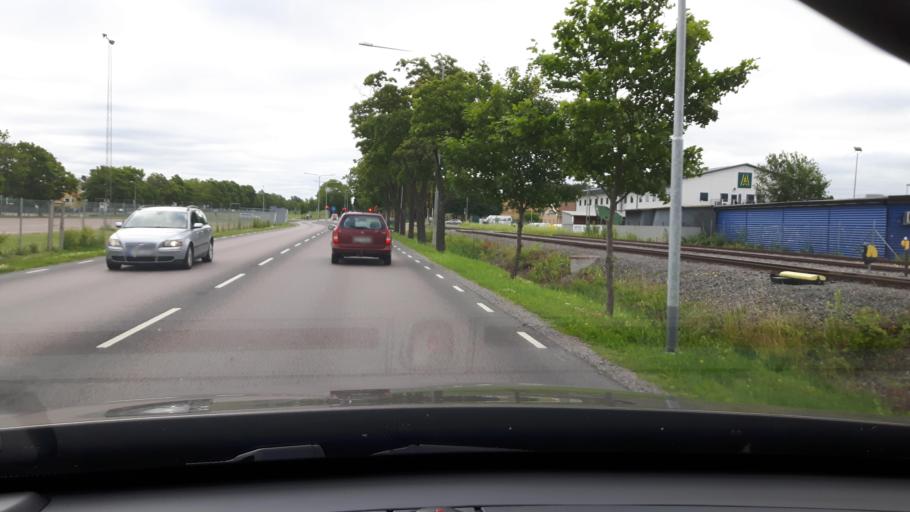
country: SE
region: Uppsala
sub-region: Uppsala Kommun
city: Uppsala
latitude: 59.8573
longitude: 17.6610
